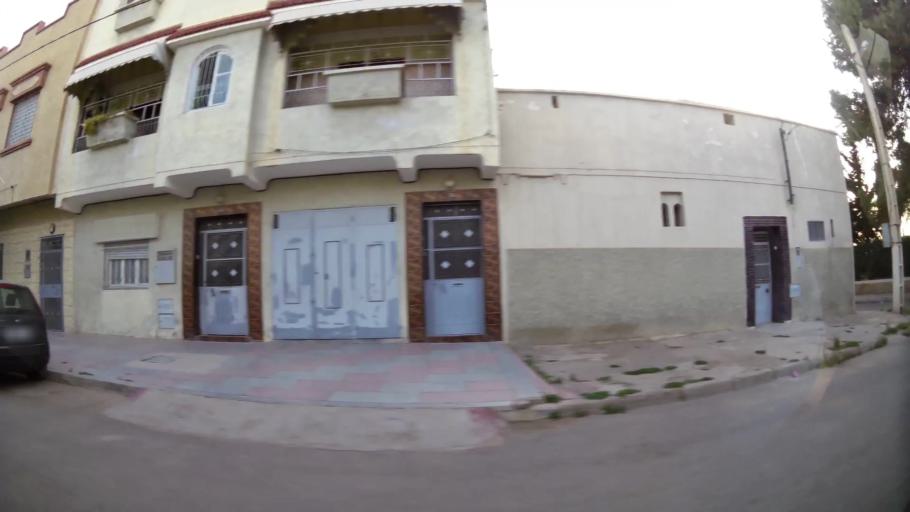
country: MA
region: Oriental
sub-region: Oujda-Angad
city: Oujda
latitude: 34.6801
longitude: -1.8883
